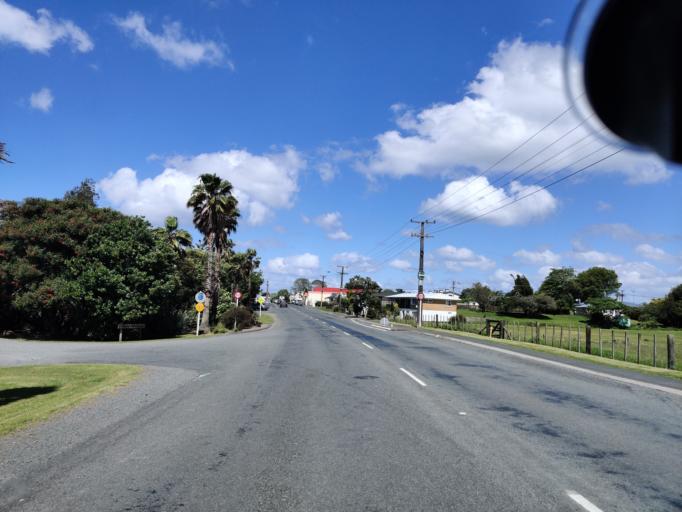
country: NZ
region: Northland
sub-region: Whangarei
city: Ruakaka
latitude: -35.9836
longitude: 174.4425
